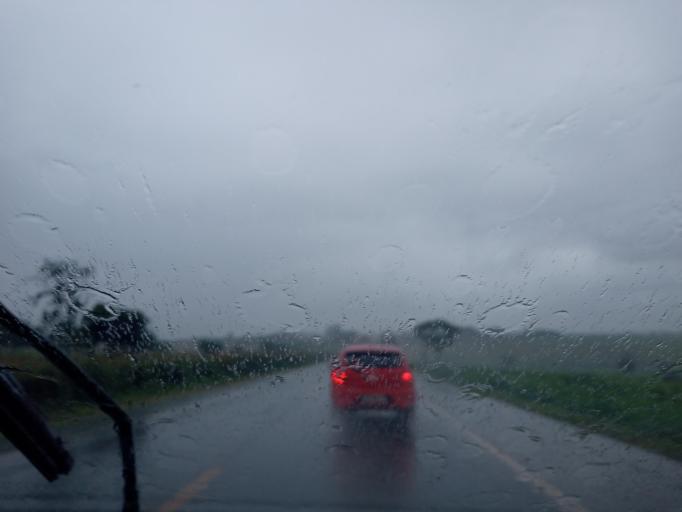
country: BR
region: Minas Gerais
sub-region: Luz
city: Luz
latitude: -19.7819
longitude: -45.6689
